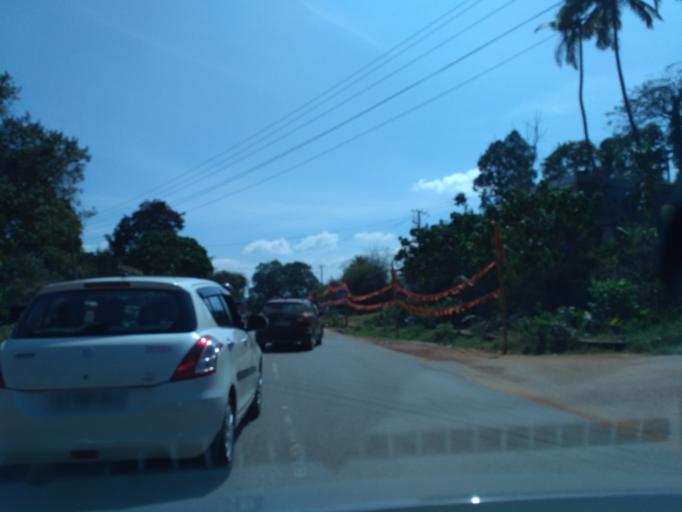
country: IN
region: Karnataka
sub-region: Dakshina Kannada
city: Puttur
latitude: 12.6948
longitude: 75.2473
